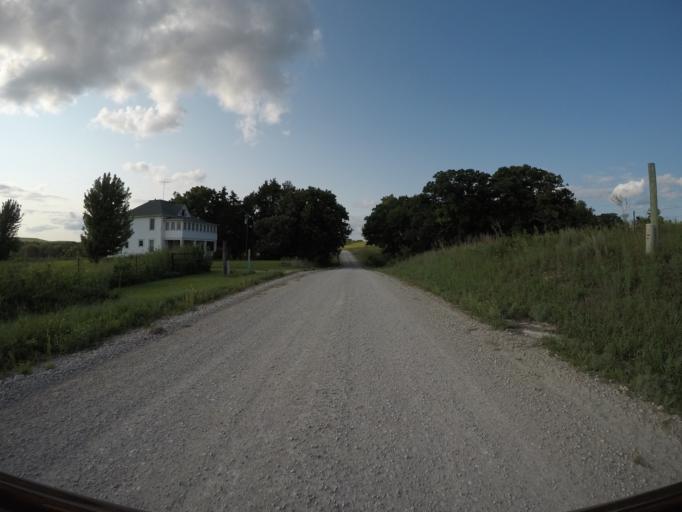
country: US
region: Kansas
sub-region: Wabaunsee County
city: Alma
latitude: 38.8948
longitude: -96.2060
